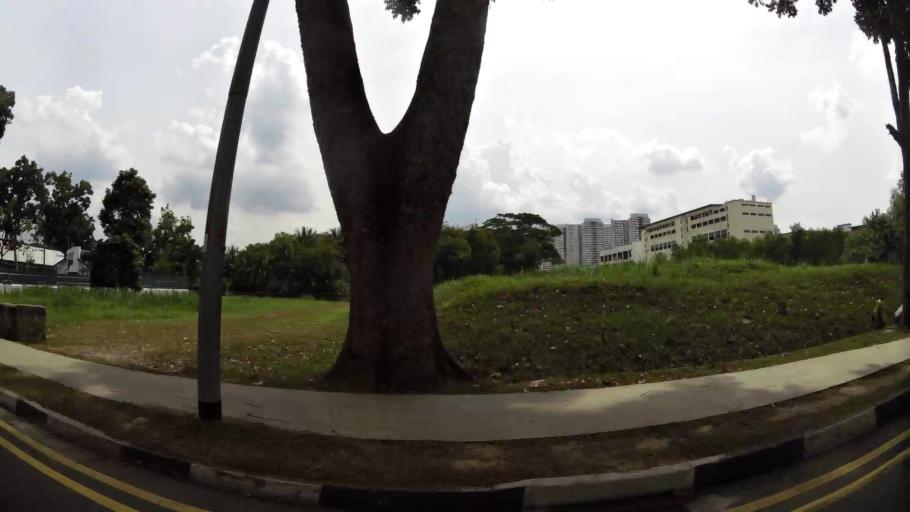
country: MY
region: Johor
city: Johor Bahru
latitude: 1.4076
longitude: 103.7548
